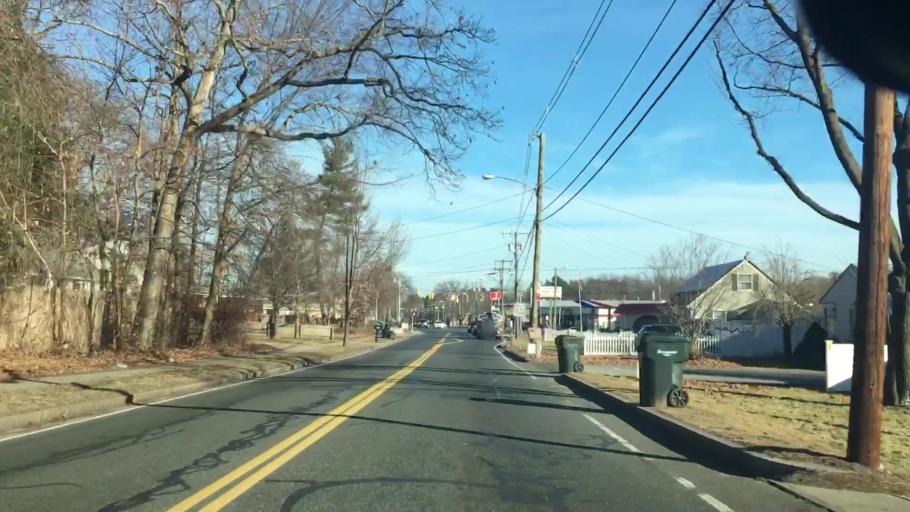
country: US
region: Massachusetts
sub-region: Hampden County
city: East Longmeadow
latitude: 42.0899
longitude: -72.5009
